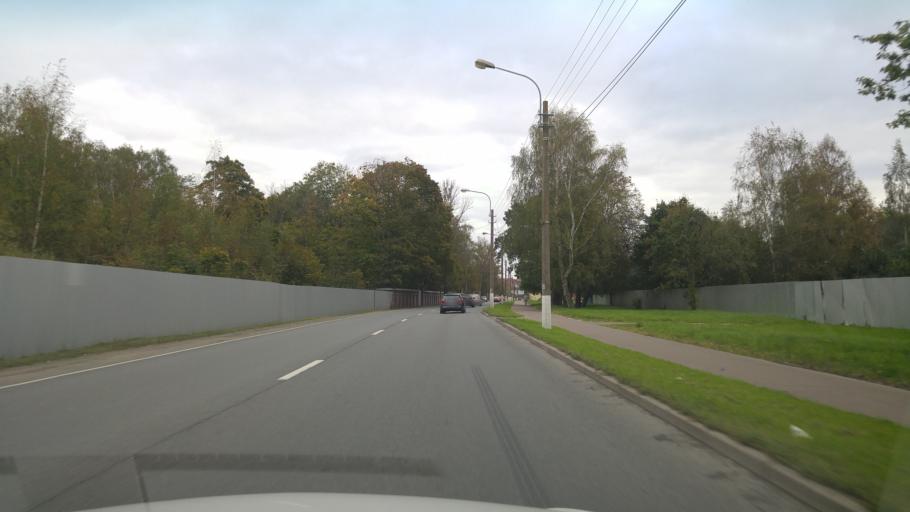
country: RU
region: St.-Petersburg
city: Kronshtadt
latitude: 60.0052
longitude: 29.7486
